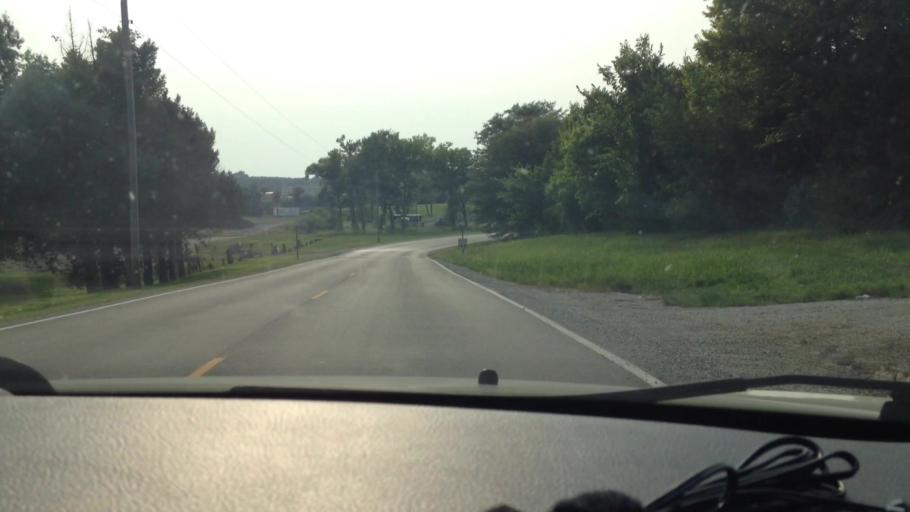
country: US
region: Missouri
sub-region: Platte County
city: Platte City
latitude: 39.3846
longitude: -94.7835
